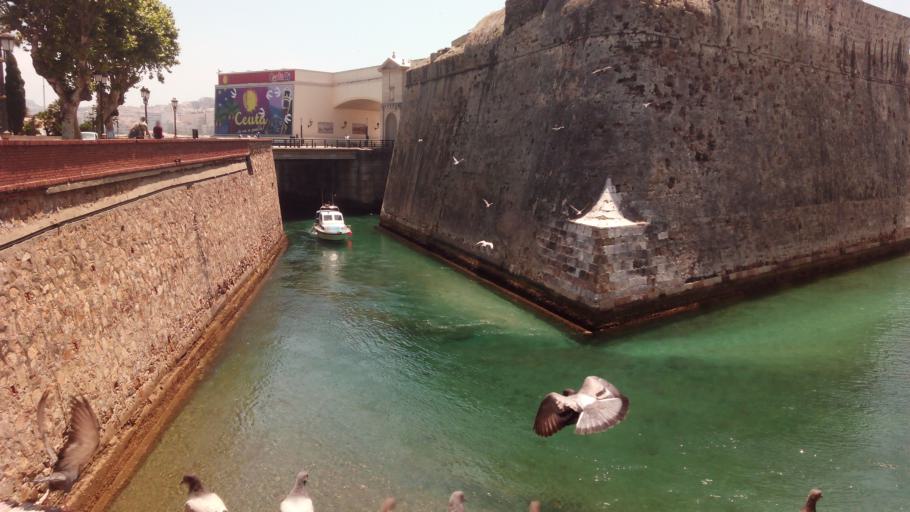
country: ES
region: Ceuta
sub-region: Ceuta
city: Ceuta
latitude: 35.8898
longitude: -5.3192
